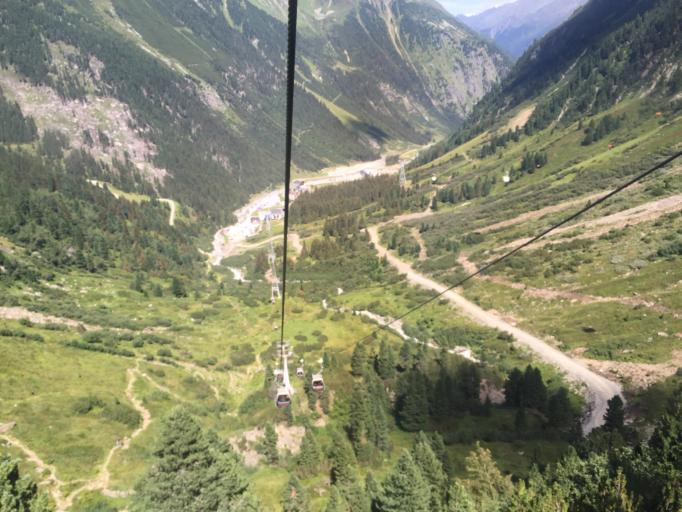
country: AT
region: Tyrol
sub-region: Politischer Bezirk Imst
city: Soelden
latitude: 47.0033
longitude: 11.1472
